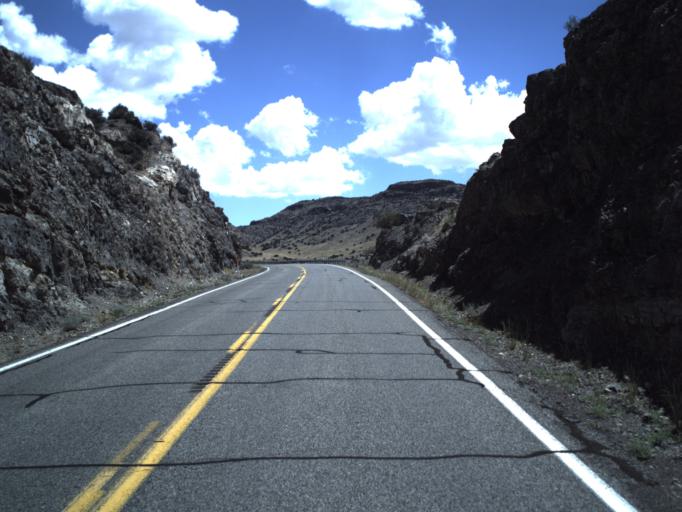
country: US
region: Utah
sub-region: Beaver County
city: Milford
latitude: 39.0714
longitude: -113.6569
